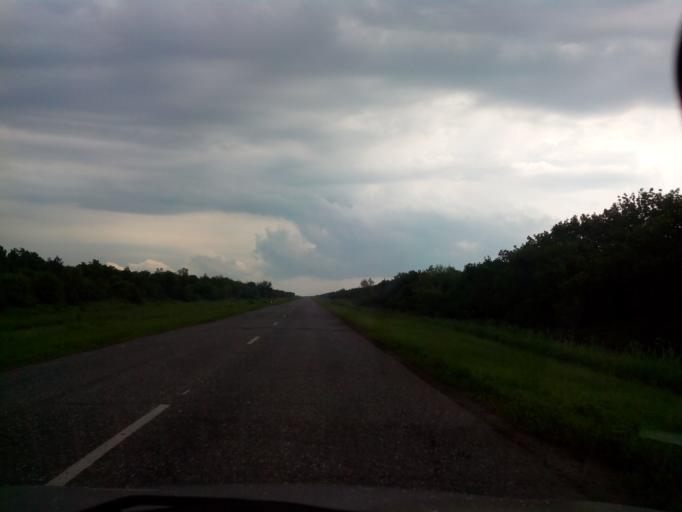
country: RU
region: Volgograd
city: Kumylzhenskaya
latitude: 49.8884
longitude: 42.8008
